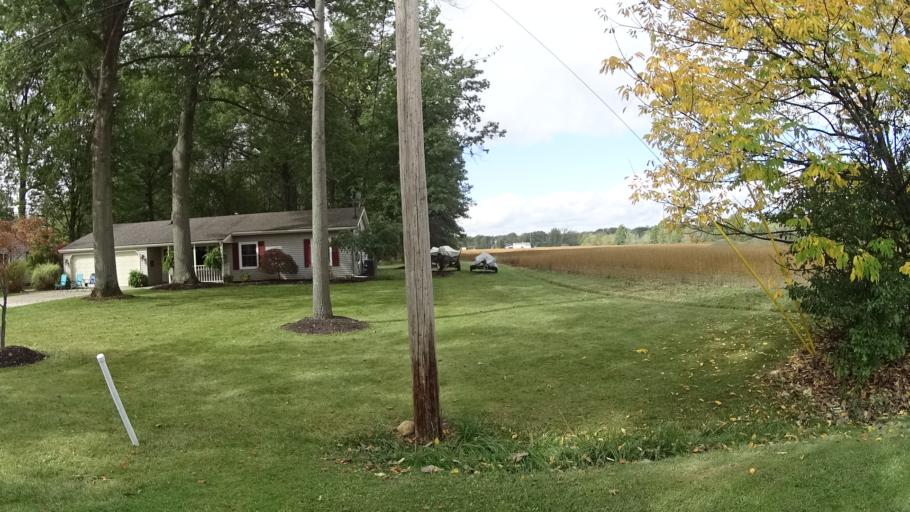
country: US
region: Ohio
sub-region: Lorain County
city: Grafton
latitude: 41.3168
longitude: -82.0623
